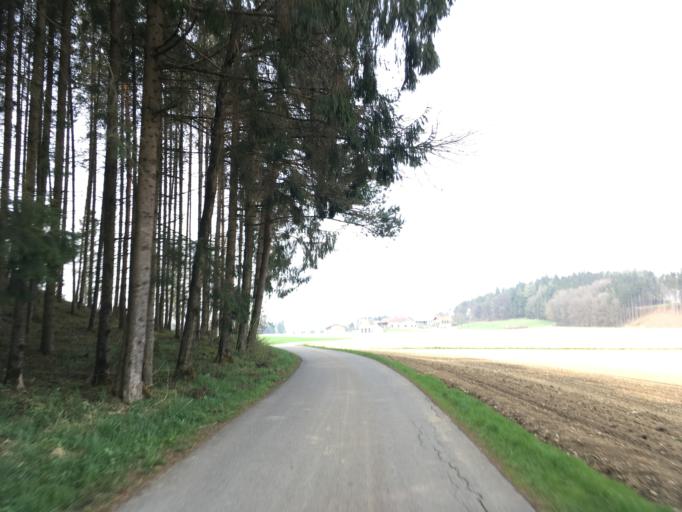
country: DE
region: Bavaria
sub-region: Upper Bavaria
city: Jettenbach
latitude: 48.1555
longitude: 12.3771
